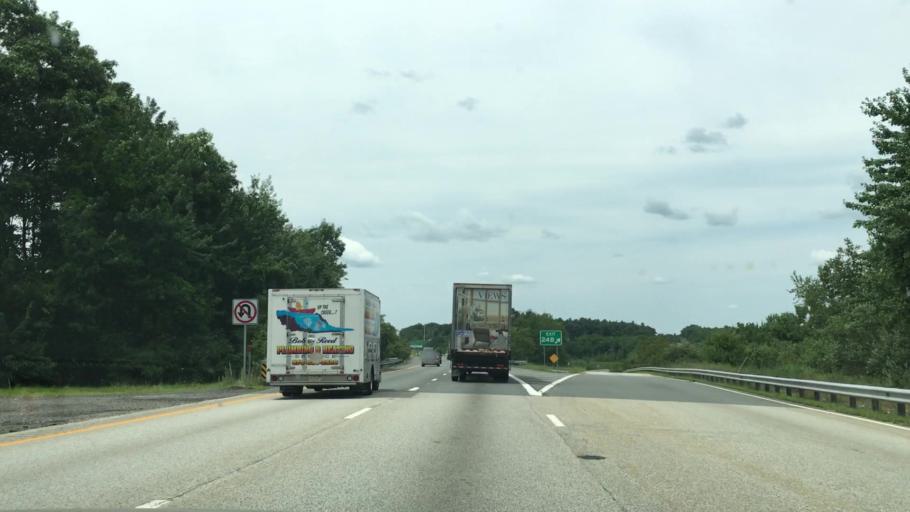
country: US
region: Massachusetts
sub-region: Worcester County
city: Westminster
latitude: 42.5584
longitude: -71.9286
